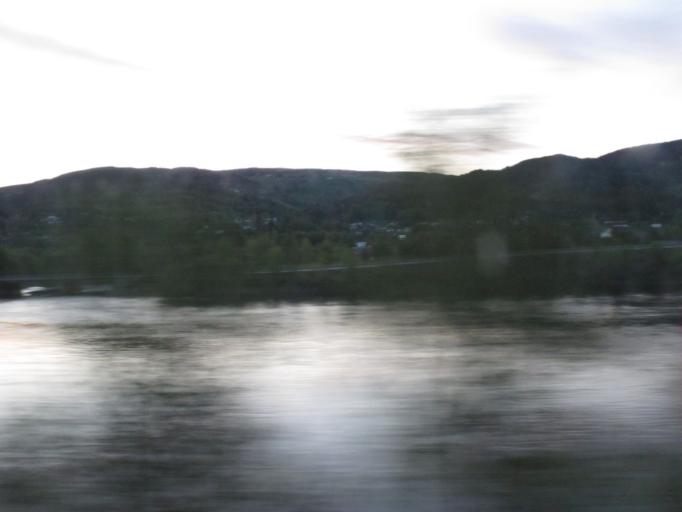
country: NO
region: Oppland
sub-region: Ringebu
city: Ringebu
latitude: 61.4514
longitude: 10.1838
